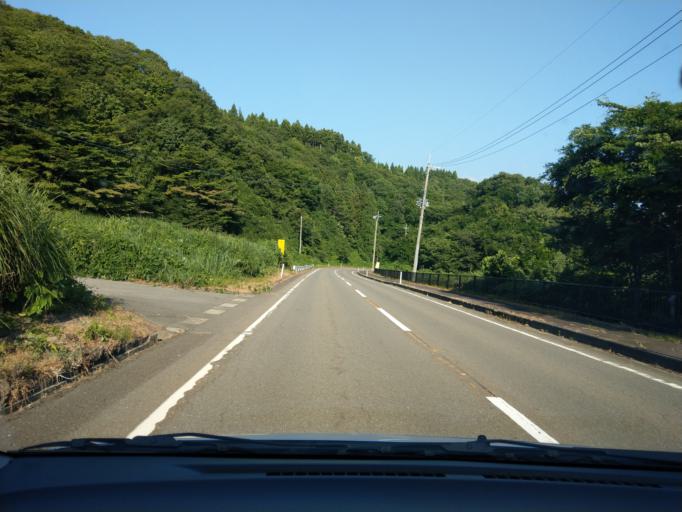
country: JP
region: Akita
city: Akita
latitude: 39.6066
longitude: 140.2041
